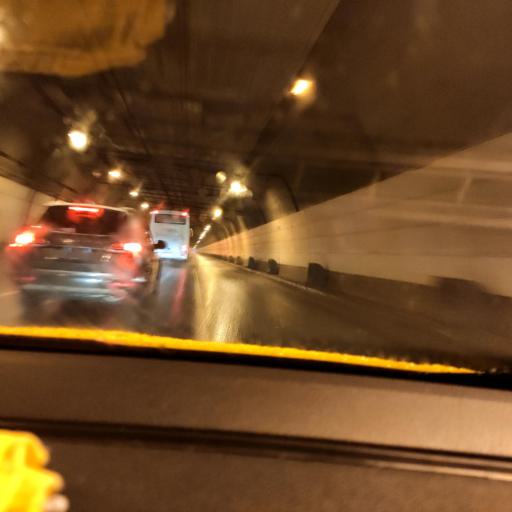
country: RU
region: Moscow
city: Rublevo
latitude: 55.7839
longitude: 37.3919
